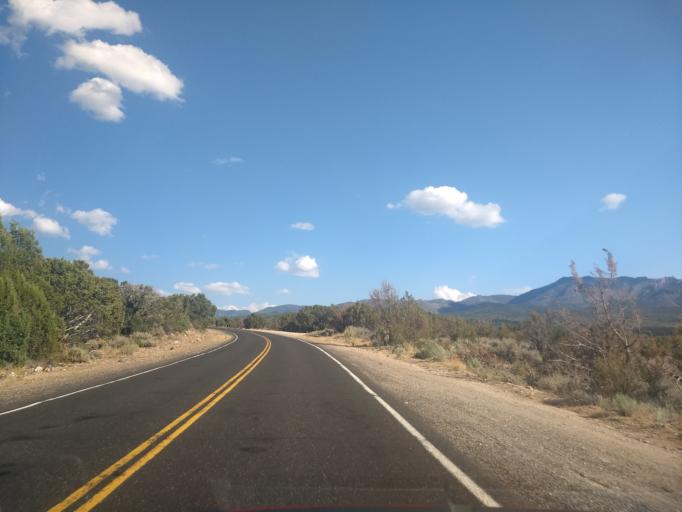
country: US
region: Utah
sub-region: Washington County
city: Enterprise
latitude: 37.4170
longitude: -113.5694
